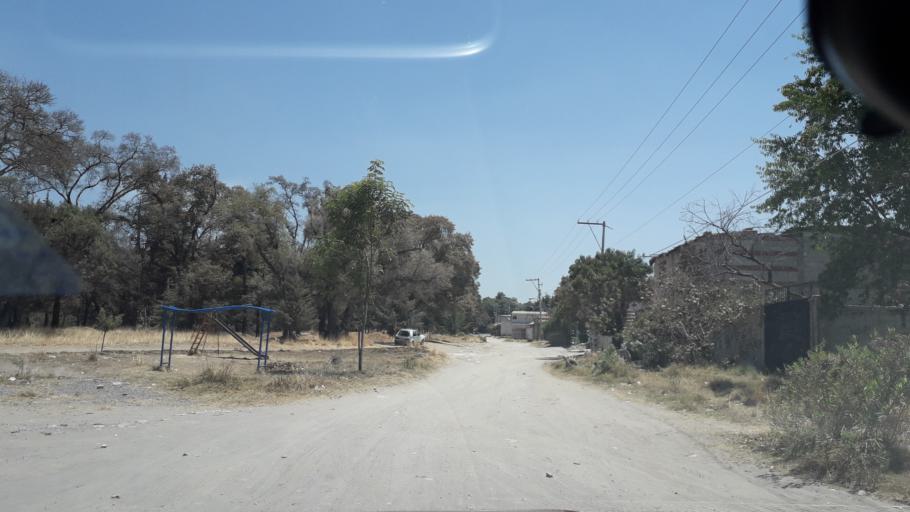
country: MX
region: Puebla
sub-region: Amozoc
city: Casa Blanca
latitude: 19.0572
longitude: -98.1177
